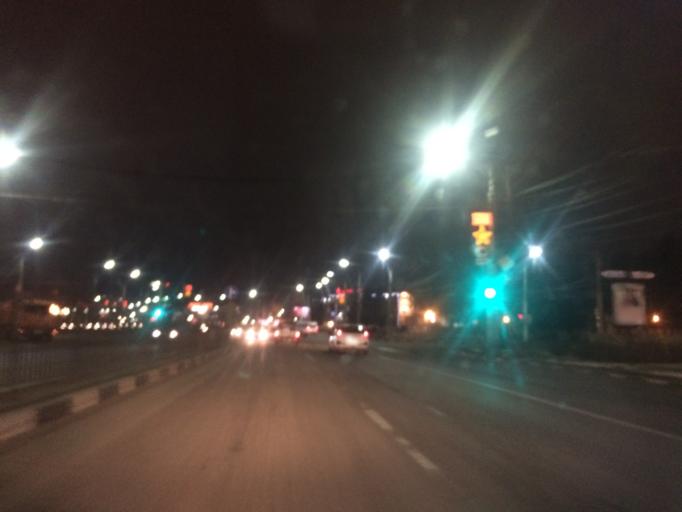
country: RU
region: Tula
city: Tula
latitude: 54.2001
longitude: 37.6137
